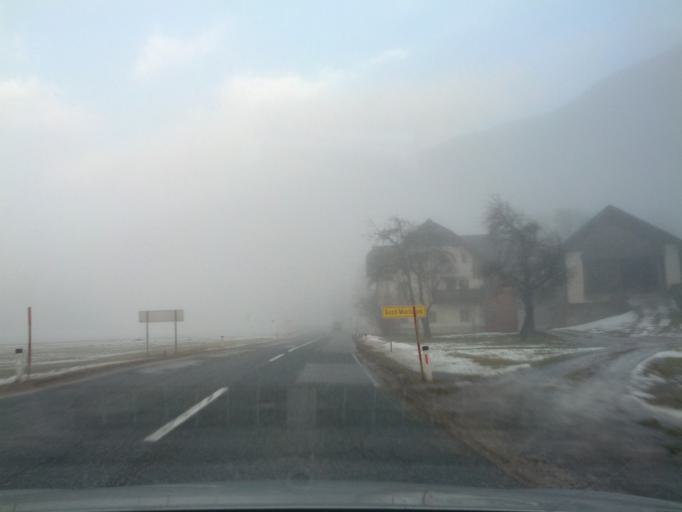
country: SI
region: Kranjska Gora
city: Mojstrana
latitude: 46.4819
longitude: 13.8503
